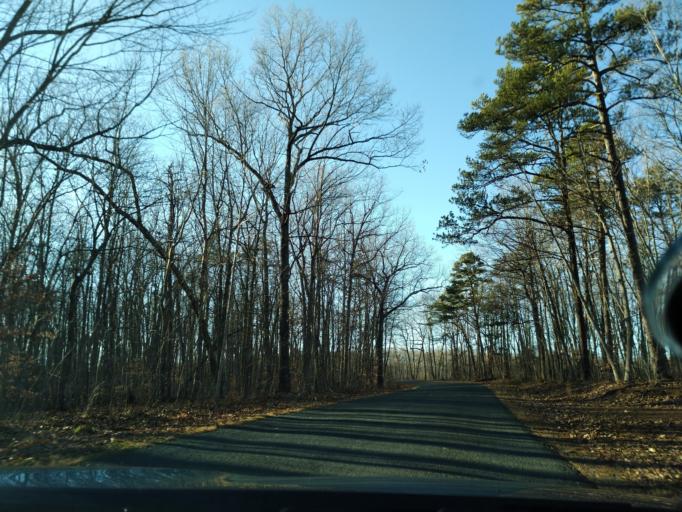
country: US
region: Virginia
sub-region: Appomattox County
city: Appomattox
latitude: 37.3957
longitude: -78.6551
